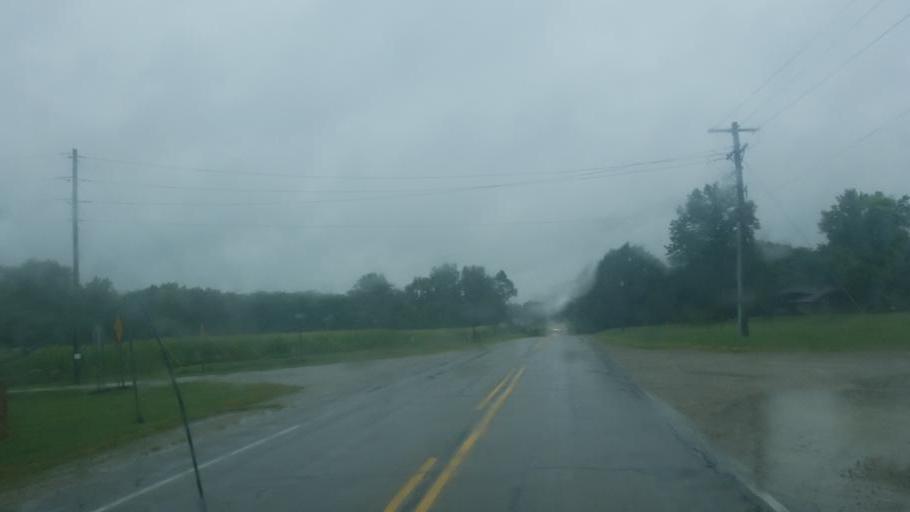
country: US
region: Indiana
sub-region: Huntington County
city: Warren
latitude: 40.6732
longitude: -85.4161
